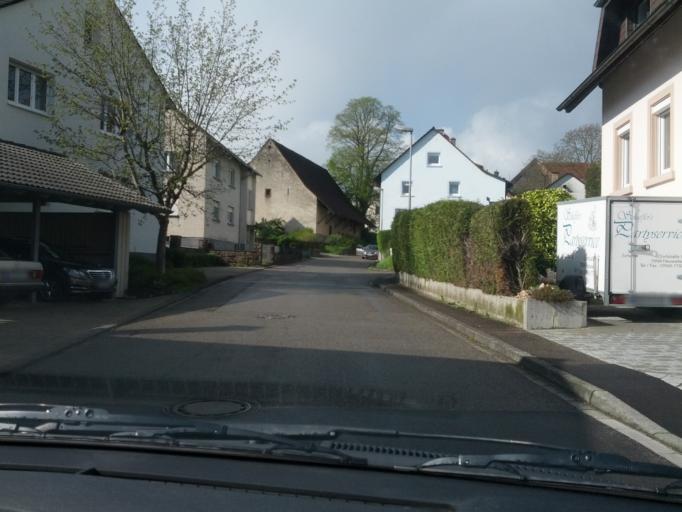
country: DE
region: Baden-Wuerttemberg
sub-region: Freiburg Region
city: Heuweiler
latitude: 48.0502
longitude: 7.9026
